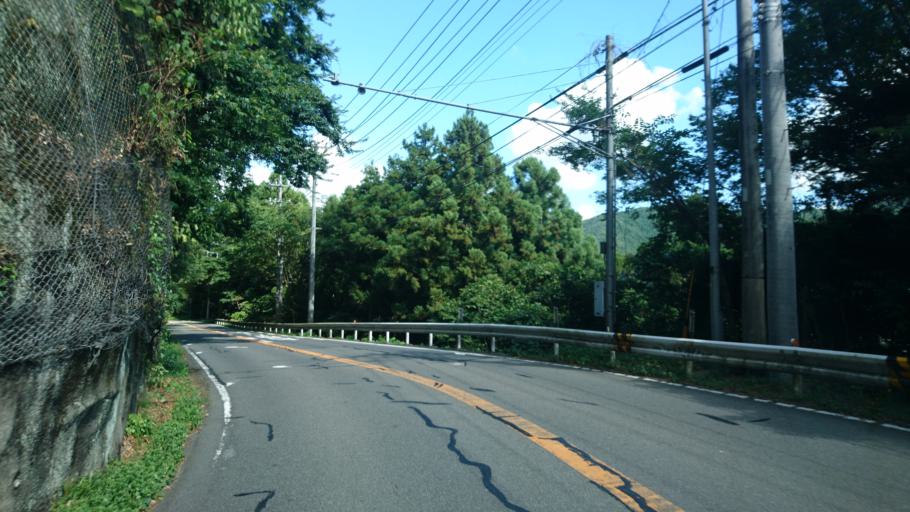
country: JP
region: Gunma
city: Omamacho-omama
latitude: 36.4563
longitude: 139.2648
